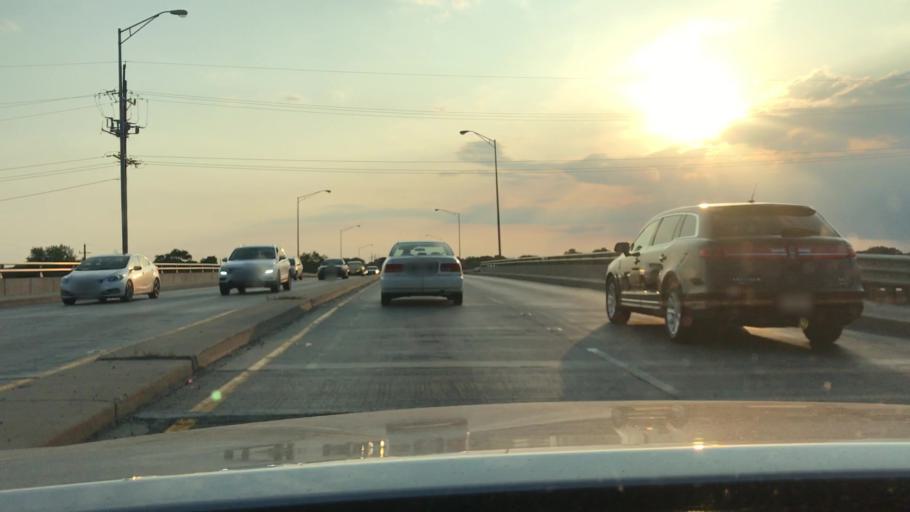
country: US
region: Illinois
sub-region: Cook County
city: Bridgeview
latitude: 41.7478
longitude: -87.8091
